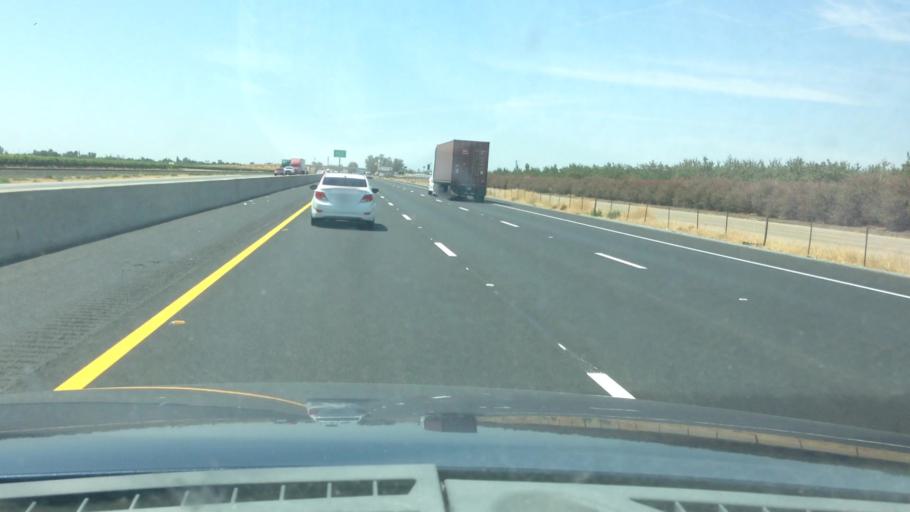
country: US
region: California
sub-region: Kern County
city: McFarland
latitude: 35.6993
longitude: -119.2326
